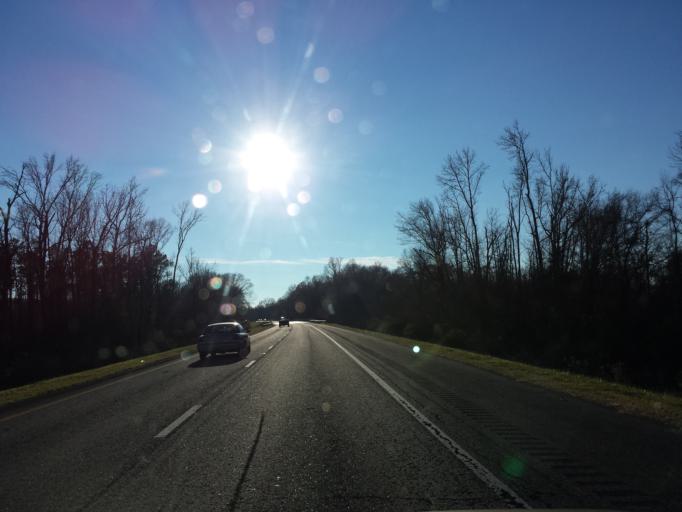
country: US
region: Alabama
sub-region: Tuscaloosa County
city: Tuscaloosa
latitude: 33.1330
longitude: -87.6394
